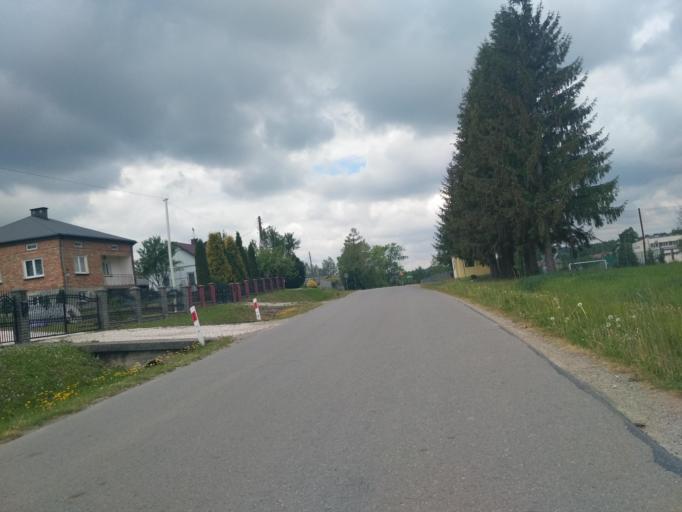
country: PL
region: Subcarpathian Voivodeship
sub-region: Powiat jasielski
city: Tarnowiec
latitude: 49.6675
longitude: 21.5676
